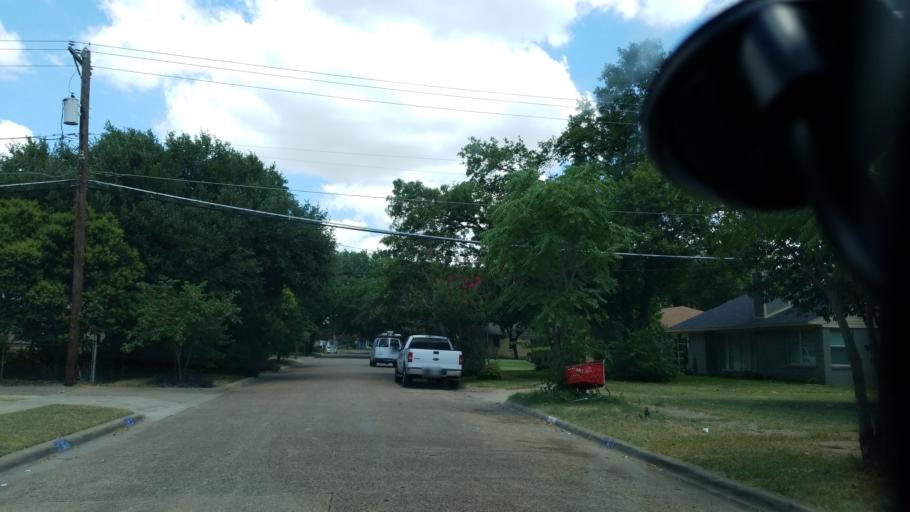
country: US
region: Texas
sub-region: Dallas County
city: Cockrell Hill
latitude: 32.7123
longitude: -96.8452
